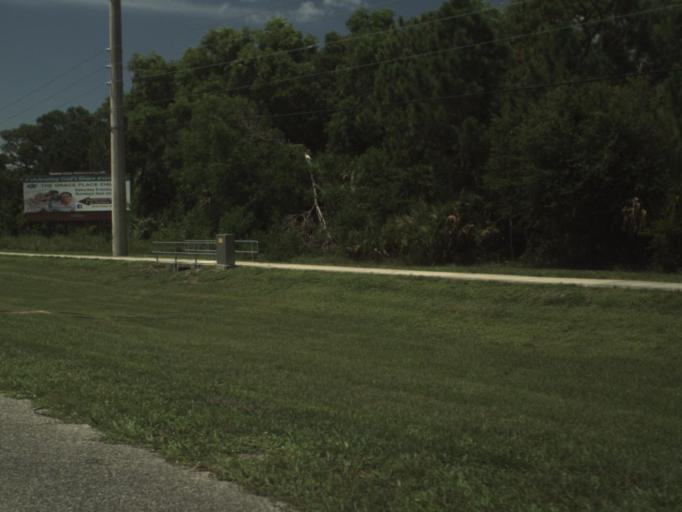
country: US
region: Florida
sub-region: Martin County
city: Port Salerno
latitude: 27.1359
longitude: -80.2082
